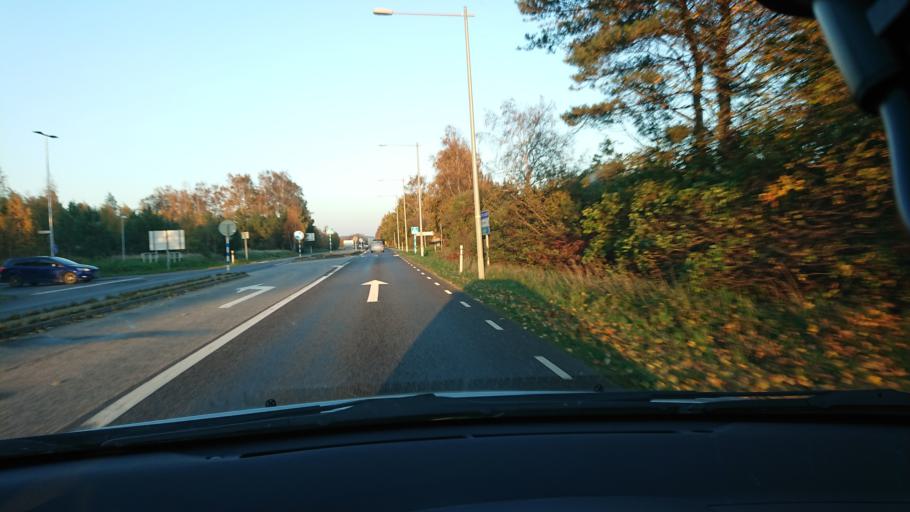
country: SE
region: Halland
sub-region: Halmstads Kommun
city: Fyllinge
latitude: 56.6790
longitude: 12.9285
